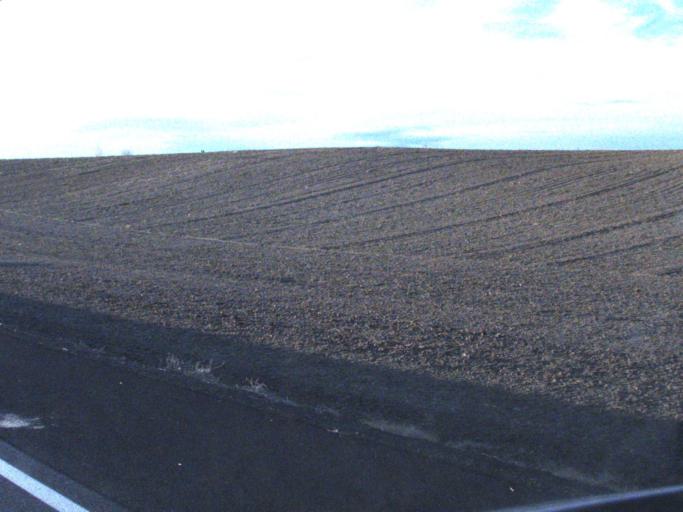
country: US
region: Washington
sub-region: Walla Walla County
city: Garrett
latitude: 46.0398
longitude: -118.6649
